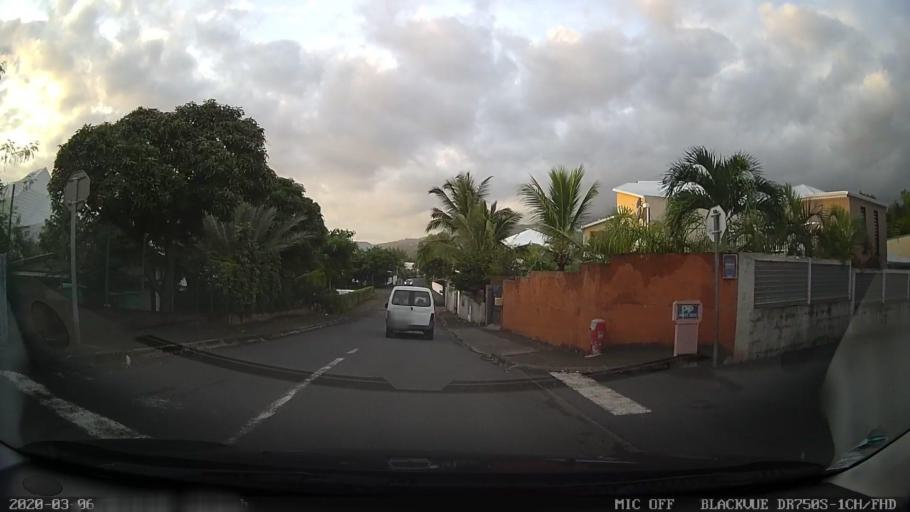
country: RE
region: Reunion
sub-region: Reunion
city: Les Avirons
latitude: -21.2690
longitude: 55.3376
